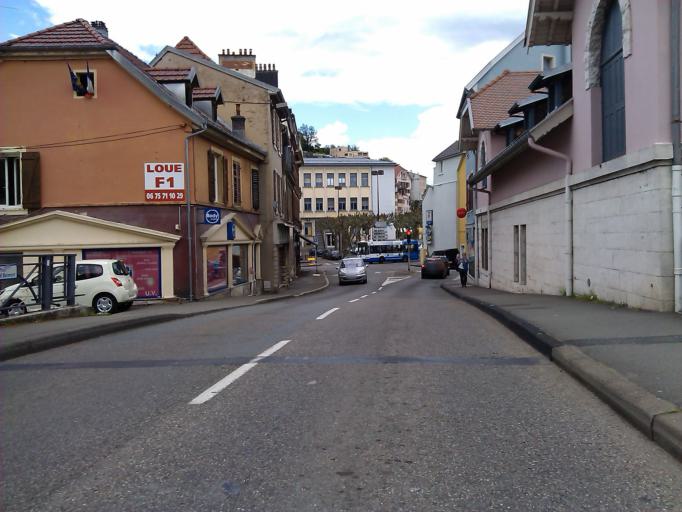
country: FR
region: Franche-Comte
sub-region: Departement du Doubs
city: Arbouans
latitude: 47.5083
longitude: 6.7932
